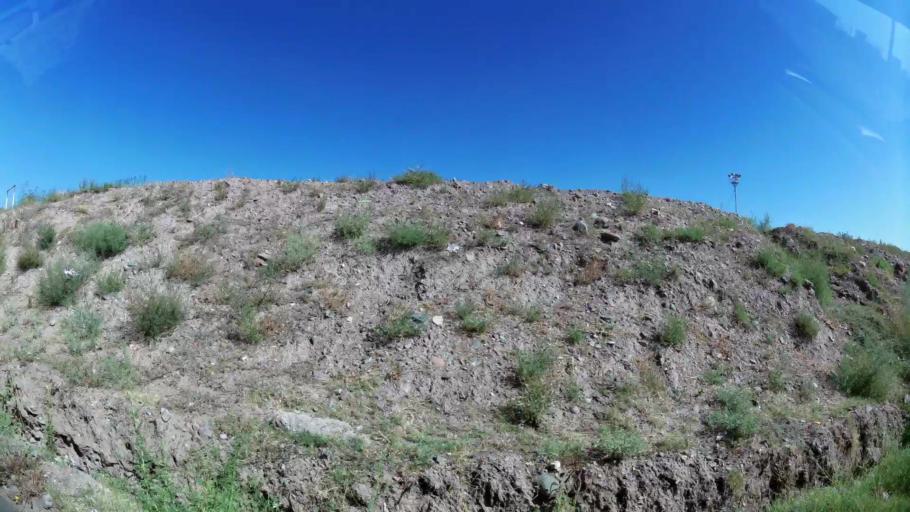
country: AR
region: Mendoza
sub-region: Departamento de Godoy Cruz
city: Godoy Cruz
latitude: -32.9115
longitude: -68.8811
